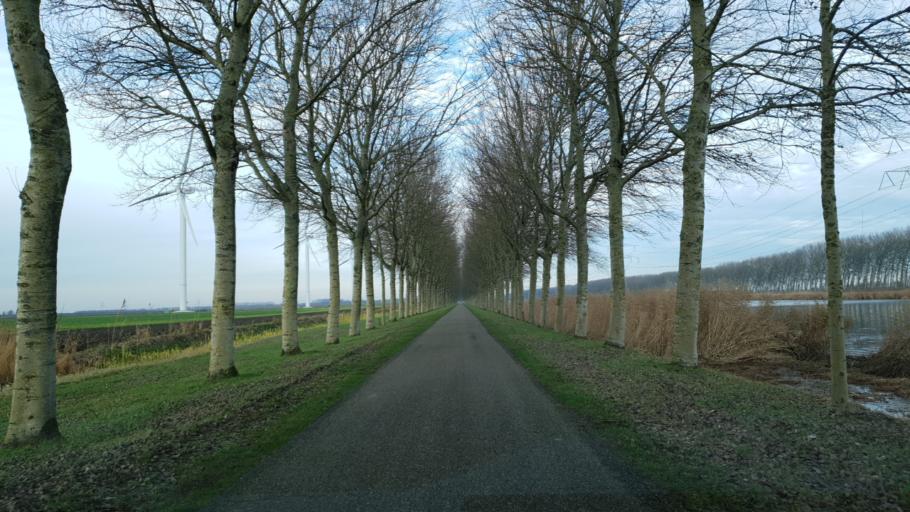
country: NL
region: North Brabant
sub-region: Gemeente Woensdrecht
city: Woensdrecht
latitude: 51.4065
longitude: 4.2339
